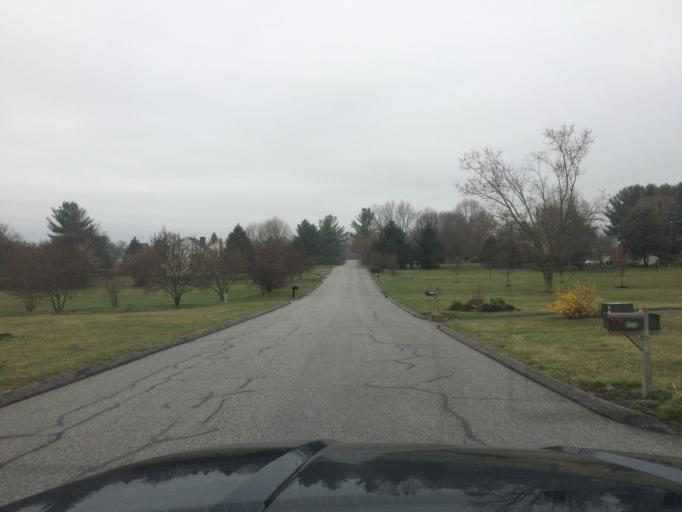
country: US
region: Maryland
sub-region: Carroll County
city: Sykesville
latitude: 39.2883
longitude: -77.0006
